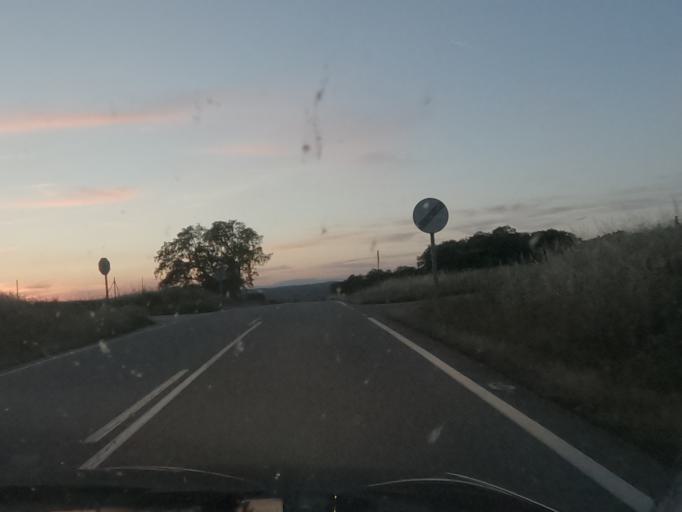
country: ES
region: Extremadura
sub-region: Provincia de Caceres
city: Piedras Albas
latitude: 39.7934
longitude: -6.9596
